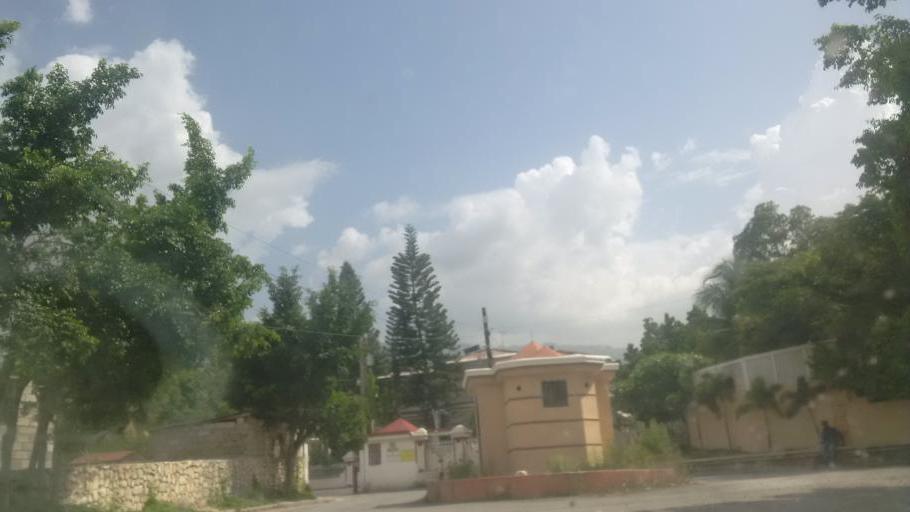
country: HT
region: Ouest
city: Petionville
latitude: 18.5275
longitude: -72.2565
